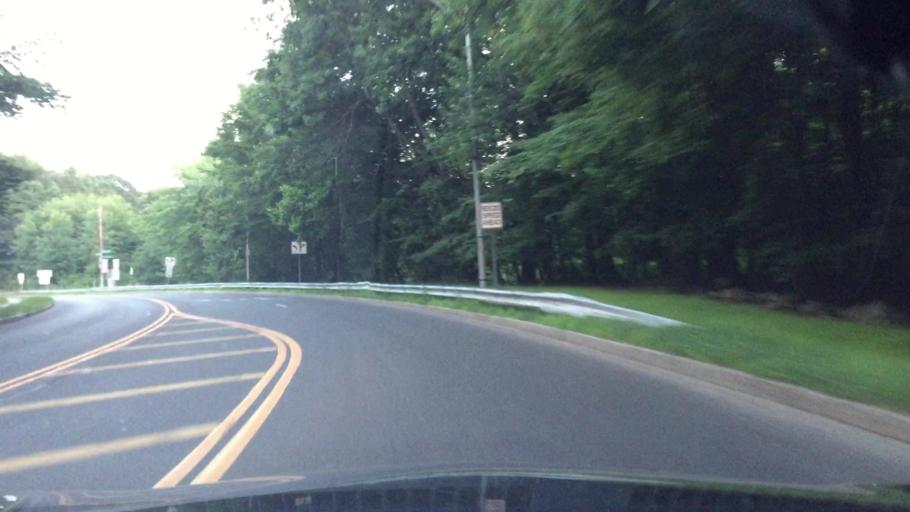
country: US
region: Connecticut
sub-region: Fairfield County
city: Darien
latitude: 41.0769
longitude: -73.4287
